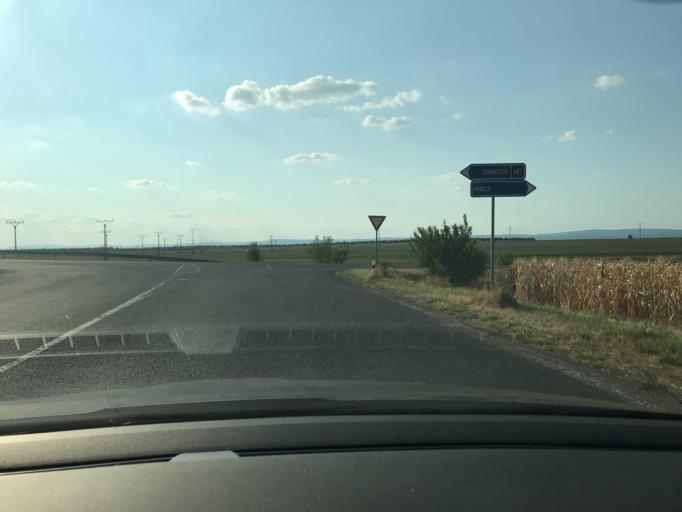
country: CZ
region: Ustecky
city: Zatec
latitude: 50.3835
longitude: 13.5675
